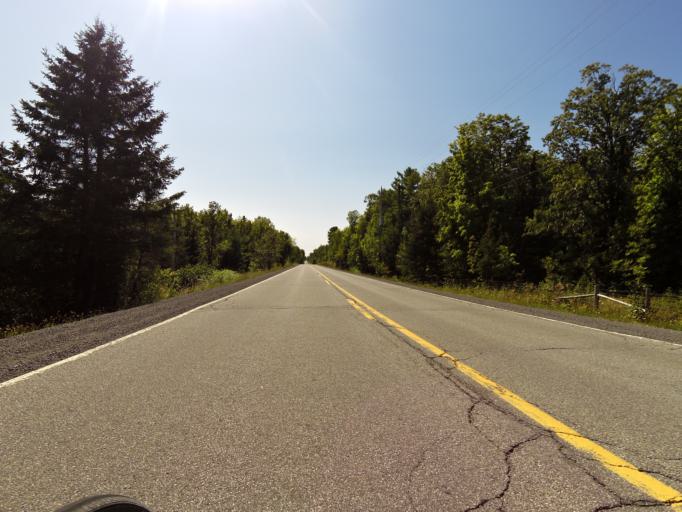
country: CA
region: Ontario
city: Bells Corners
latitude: 45.3866
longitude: -75.9417
